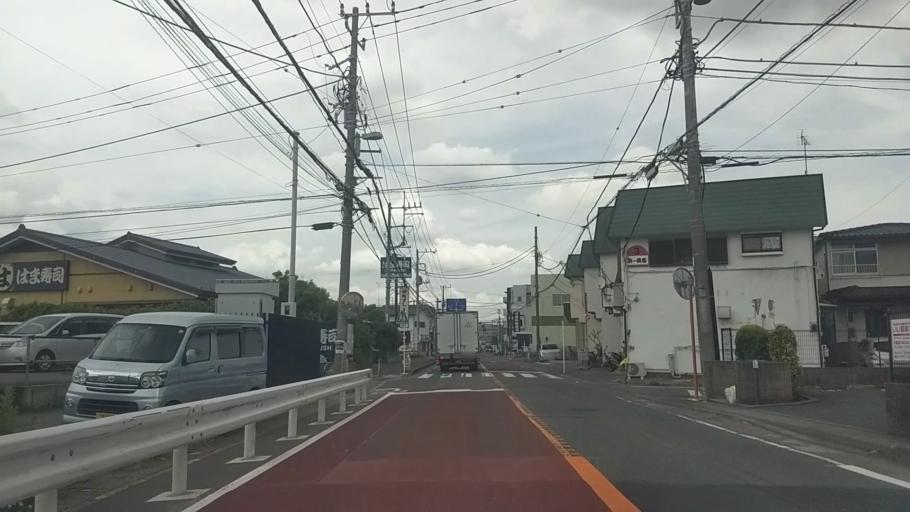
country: JP
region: Kanagawa
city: Fujisawa
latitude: 35.3295
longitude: 139.5095
